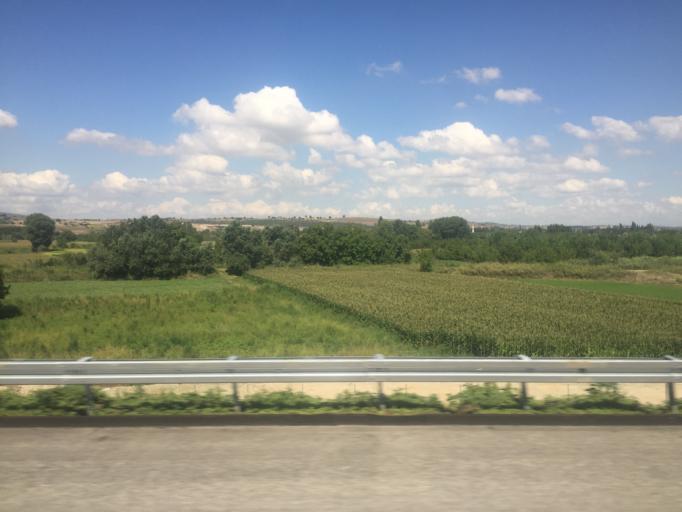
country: TR
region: Balikesir
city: Gobel
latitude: 39.9882
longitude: 28.1860
